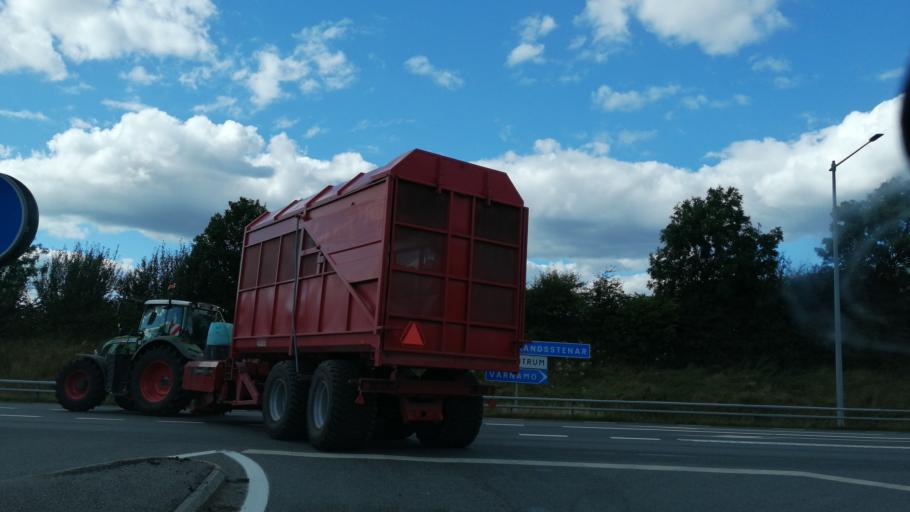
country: SE
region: Joenkoeping
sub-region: Gislaveds Kommun
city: Reftele
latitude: 57.1729
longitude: 13.5989
